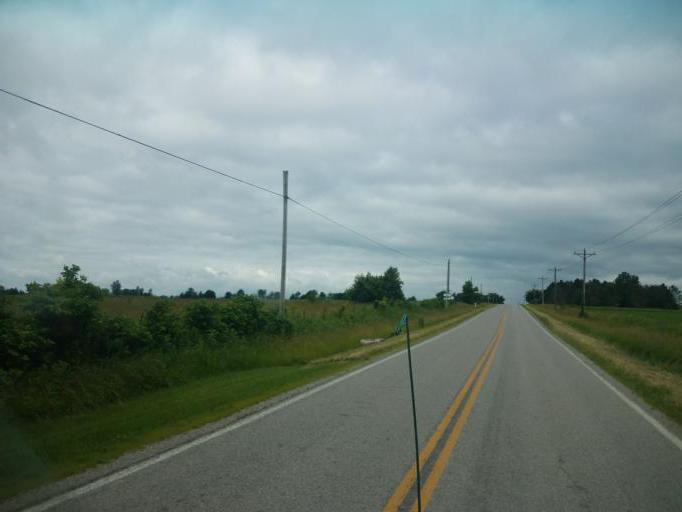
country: US
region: Ohio
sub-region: Union County
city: Richwood
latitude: 40.4158
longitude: -83.4742
